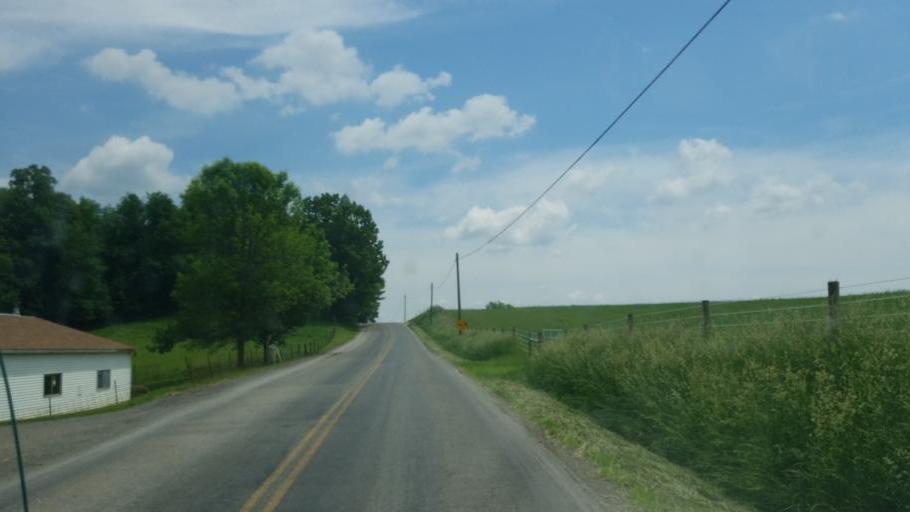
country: US
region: Ohio
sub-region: Tuscarawas County
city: Sugarcreek
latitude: 40.4522
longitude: -81.7727
